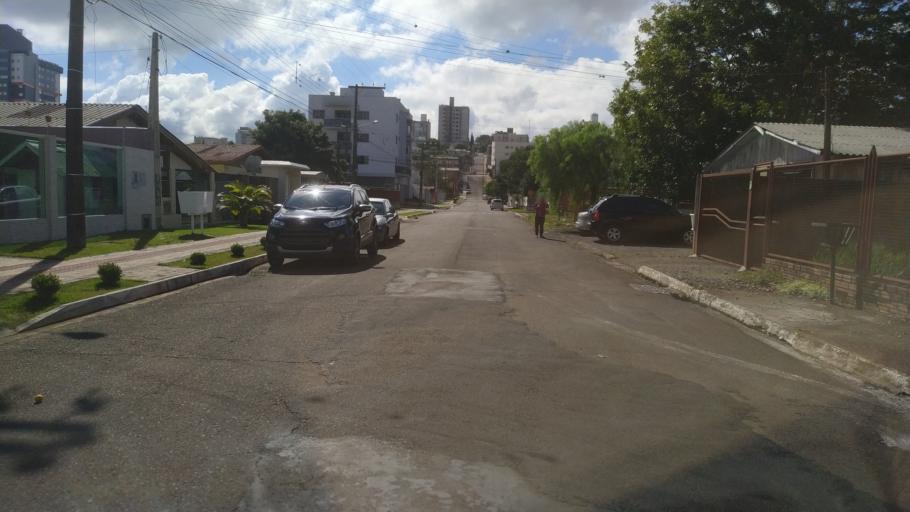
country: BR
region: Santa Catarina
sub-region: Chapeco
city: Chapeco
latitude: -27.0975
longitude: -52.6342
